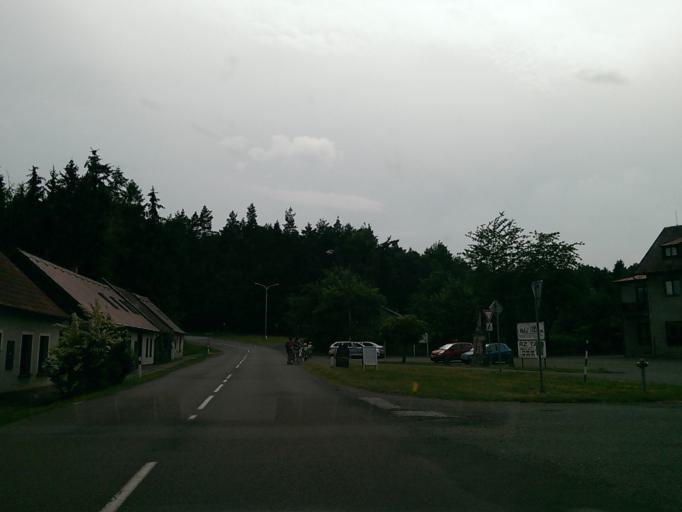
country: CZ
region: Kralovehradecky
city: Horice
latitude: 50.3850
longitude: 15.6393
